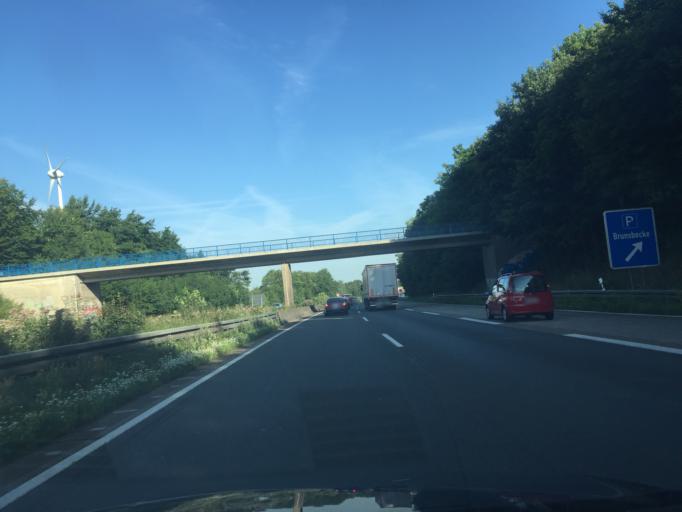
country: DE
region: North Rhine-Westphalia
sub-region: Regierungsbezirk Arnsberg
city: Nachrodt-Wiblingwerde
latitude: 51.3206
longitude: 7.5396
